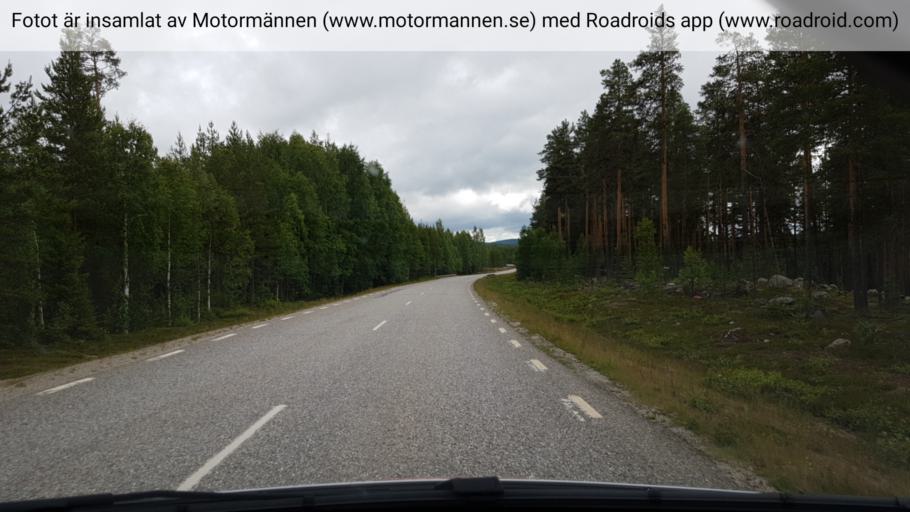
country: SE
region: Vaesterbotten
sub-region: Norsjo Kommun
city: Norsjoe
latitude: 64.6730
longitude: 19.2583
